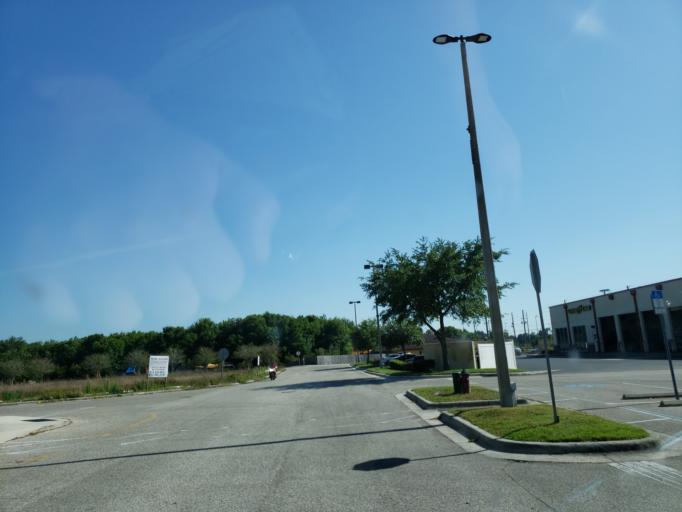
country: US
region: Florida
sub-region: Hillsborough County
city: Sun City Center
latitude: 27.7894
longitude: -82.3340
